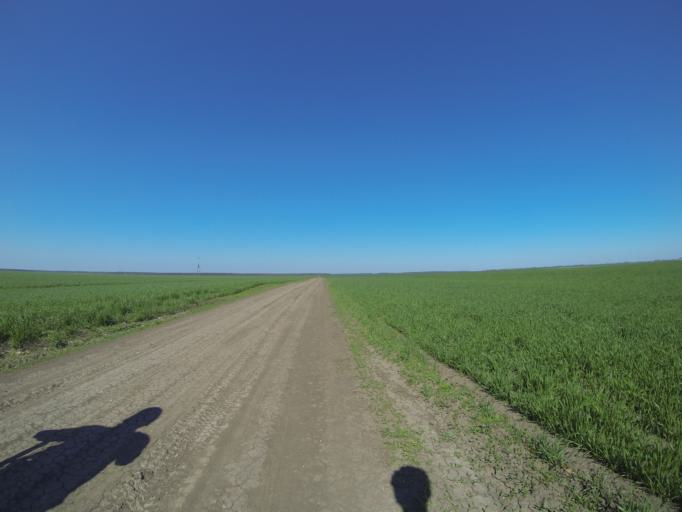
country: RO
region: Dolj
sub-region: Comuna Caloparu
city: Salcuta
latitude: 44.1639
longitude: 23.6663
